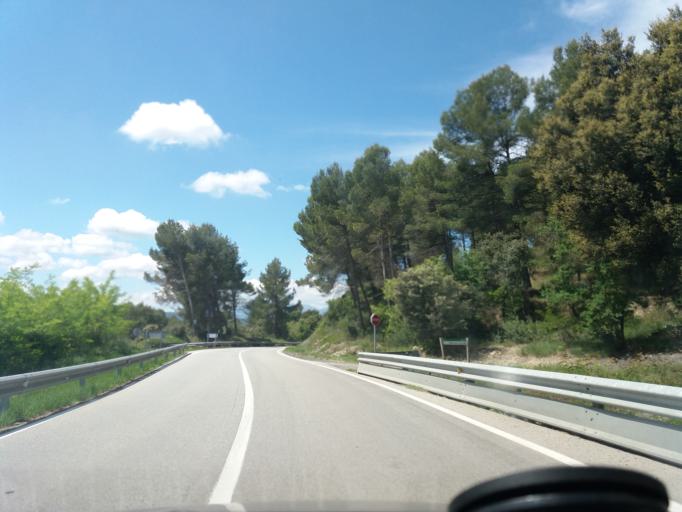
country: ES
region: Catalonia
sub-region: Provincia de Barcelona
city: Artes
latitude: 41.7742
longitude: 1.9625
